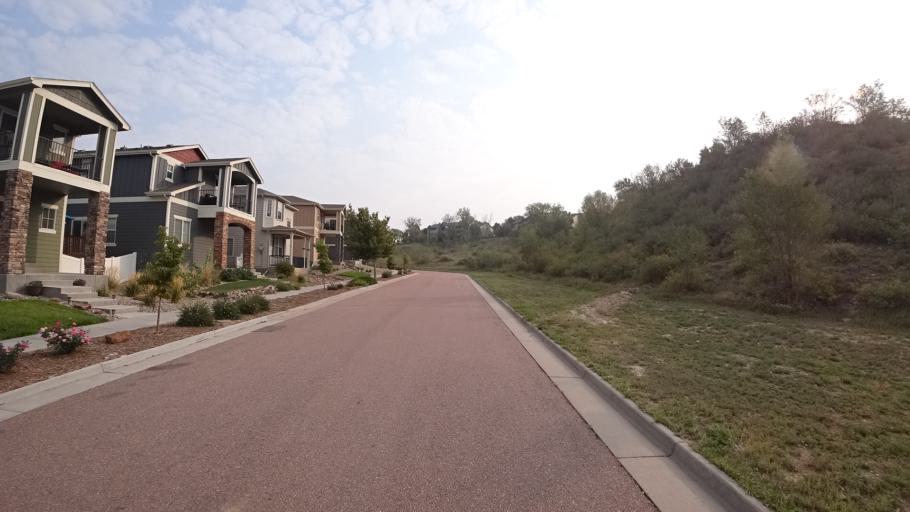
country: US
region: Colorado
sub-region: El Paso County
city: Stratmoor
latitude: 38.8044
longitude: -104.7838
